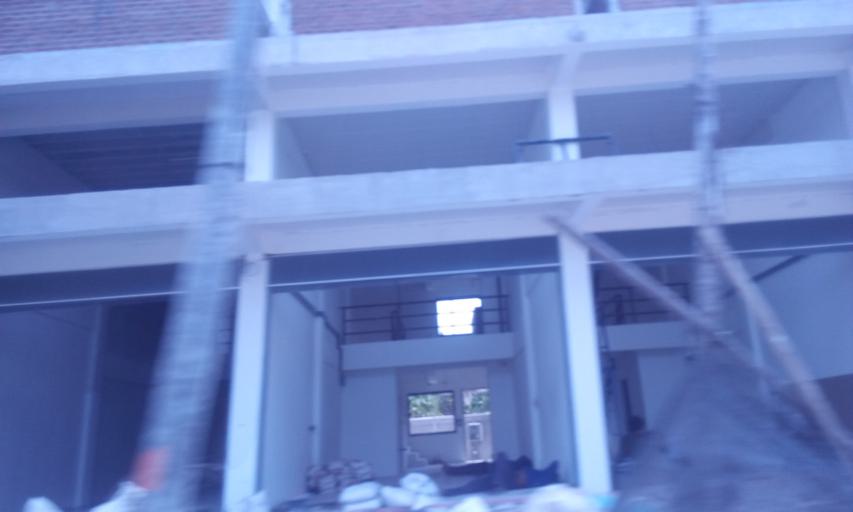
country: TH
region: Chachoengsao
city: Chachoengsao
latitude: 13.6931
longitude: 101.0771
